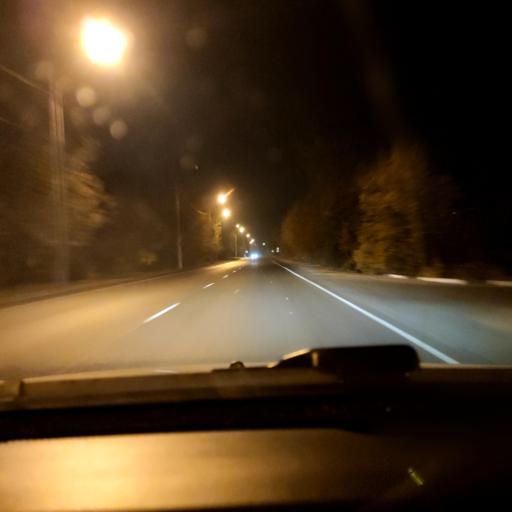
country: RU
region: Voronezj
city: Maslovka
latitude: 51.5843
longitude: 39.1666
